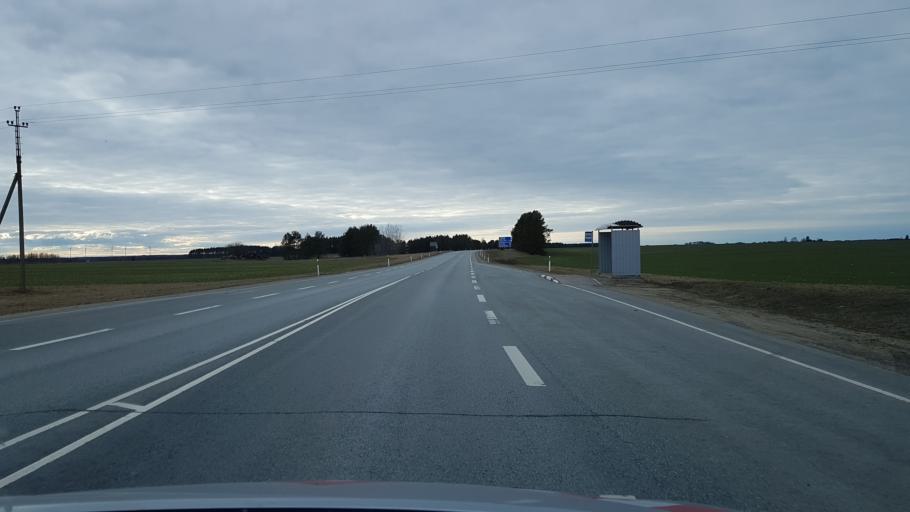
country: EE
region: Ida-Virumaa
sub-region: Puessi linn
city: Pussi
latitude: 59.4036
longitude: 27.0718
